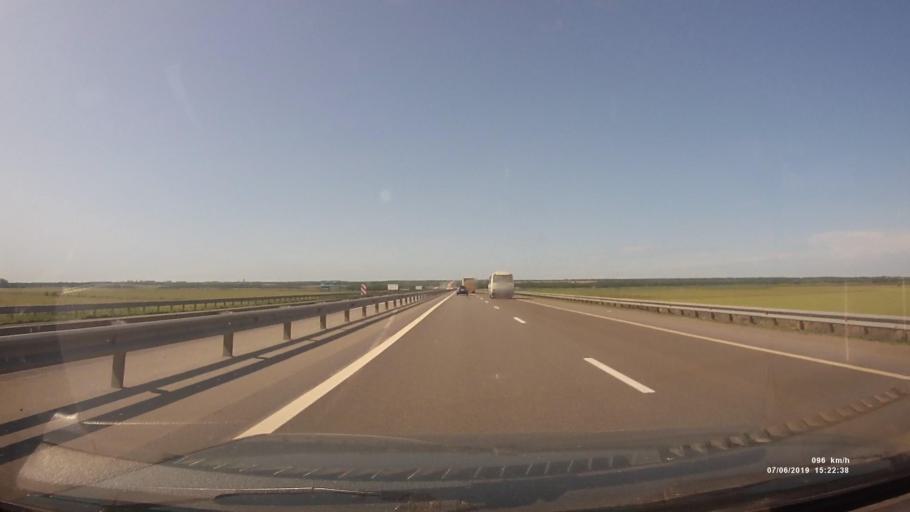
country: RU
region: Rostov
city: Grushevskaya
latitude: 47.4516
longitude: 39.9743
